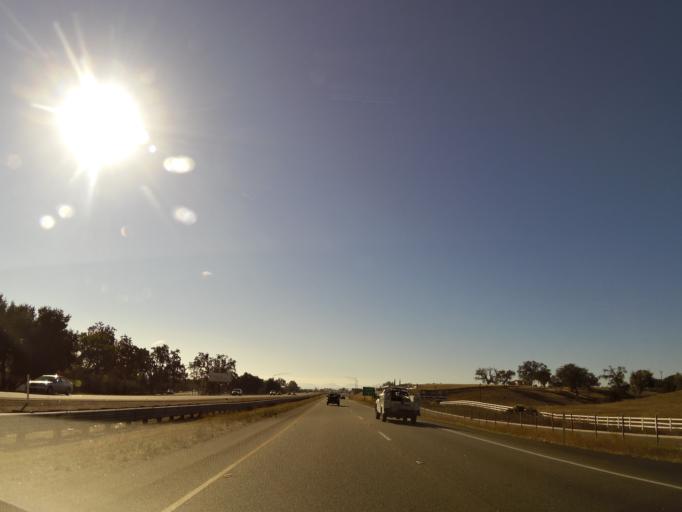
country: US
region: California
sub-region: San Luis Obispo County
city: Paso Robles
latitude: 35.5951
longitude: -120.6955
